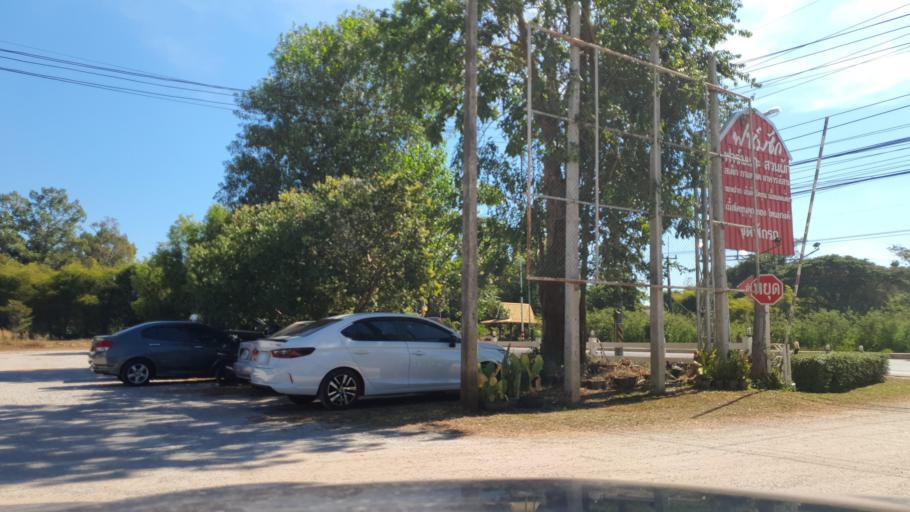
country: TH
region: Sakon Nakhon
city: Sakon Nakhon
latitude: 17.0862
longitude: 104.1856
